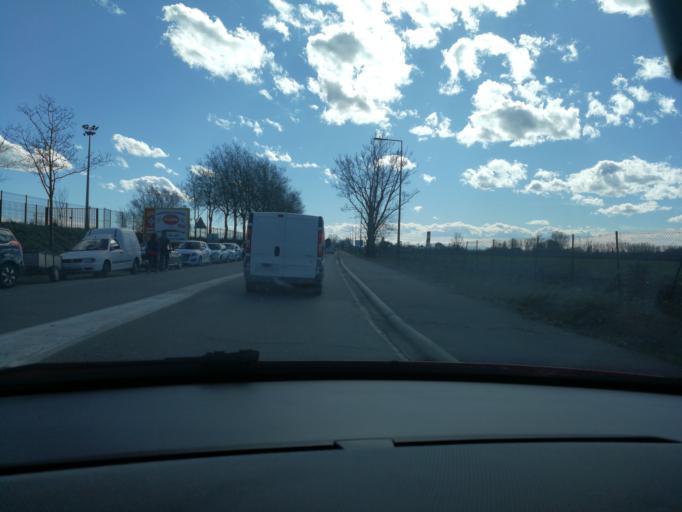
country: FR
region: Midi-Pyrenees
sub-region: Departement de la Haute-Garonne
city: Portet-sur-Garonne
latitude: 43.5413
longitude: 1.3903
